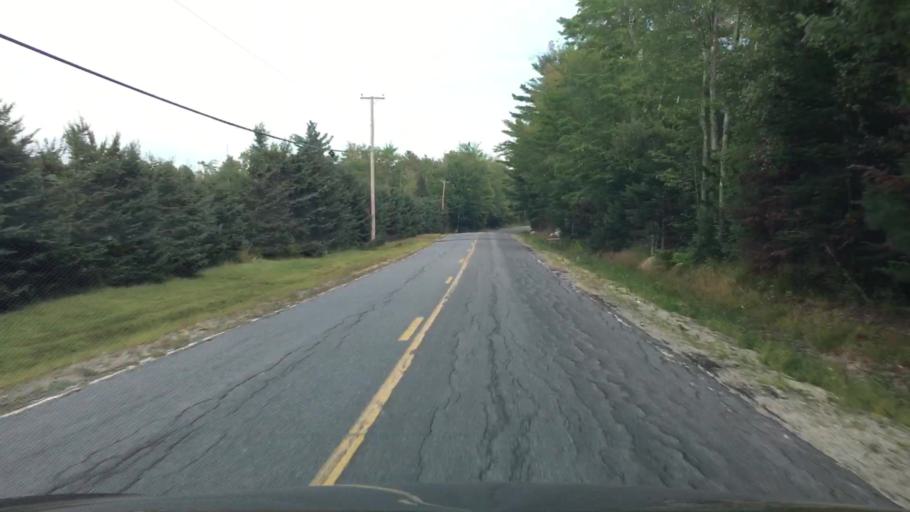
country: US
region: Maine
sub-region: Hancock County
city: Surry
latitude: 44.4993
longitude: -68.5503
